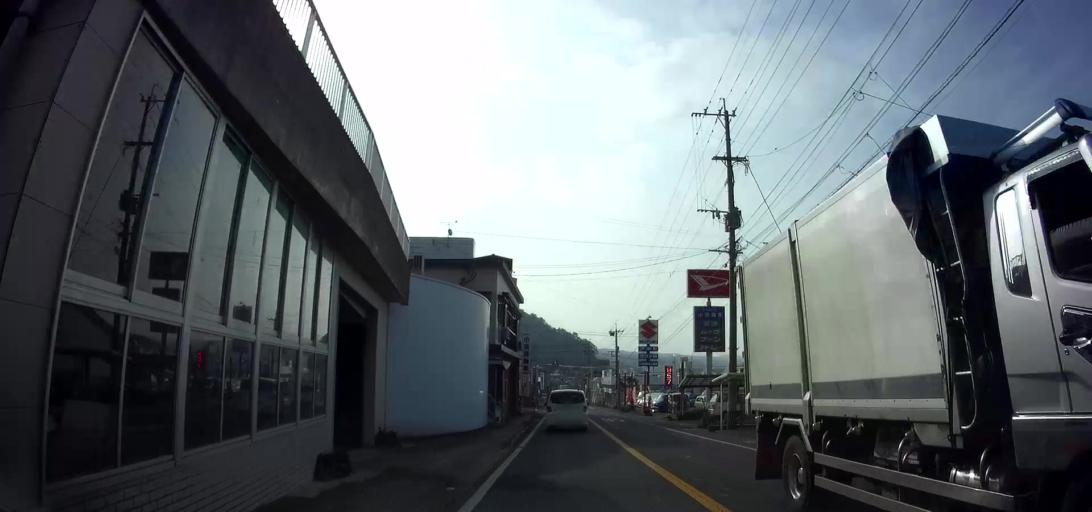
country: JP
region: Nagasaki
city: Shimabara
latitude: 32.7466
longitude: 130.2104
